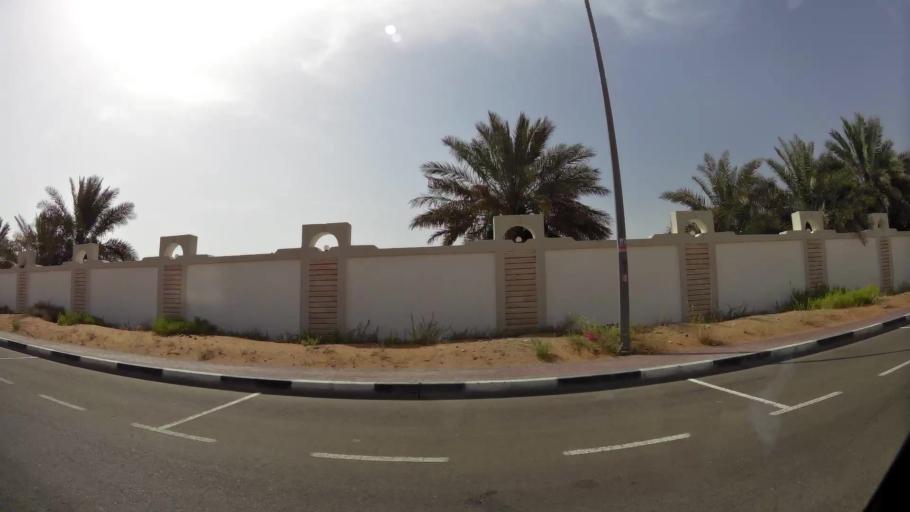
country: AE
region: Abu Dhabi
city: Al Ain
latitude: 24.1542
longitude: 55.6856
